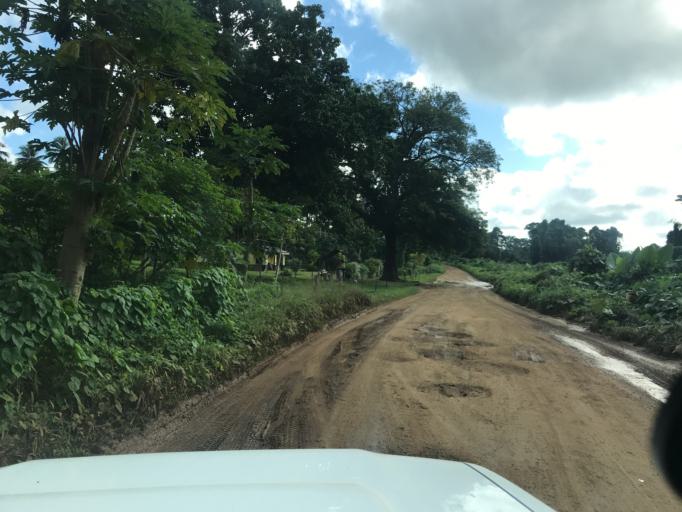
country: VU
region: Sanma
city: Luganville
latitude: -15.4951
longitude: 167.0893
